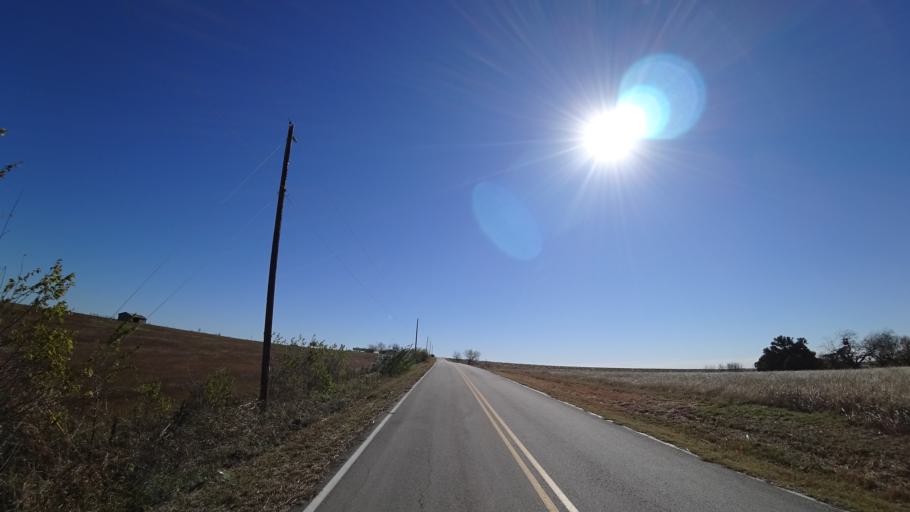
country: US
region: Texas
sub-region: Travis County
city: Garfield
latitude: 30.1065
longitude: -97.6454
